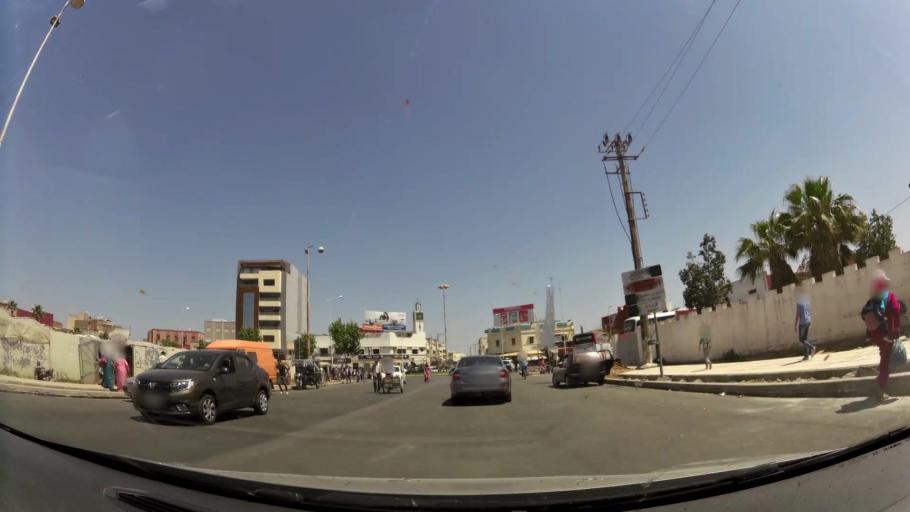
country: MA
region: Rabat-Sale-Zemmour-Zaer
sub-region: Khemisset
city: Khemisset
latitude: 33.8252
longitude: -6.0713
